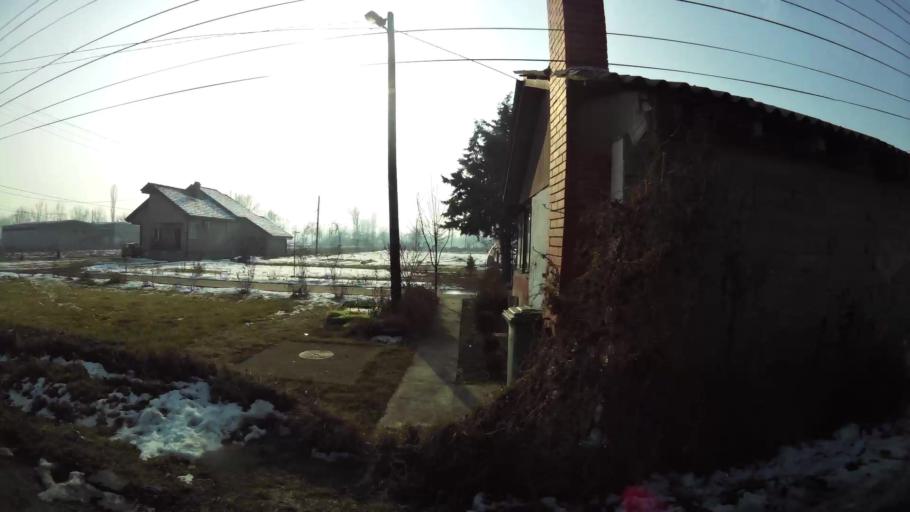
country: MK
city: Kadino
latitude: 41.9635
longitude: 21.5951
